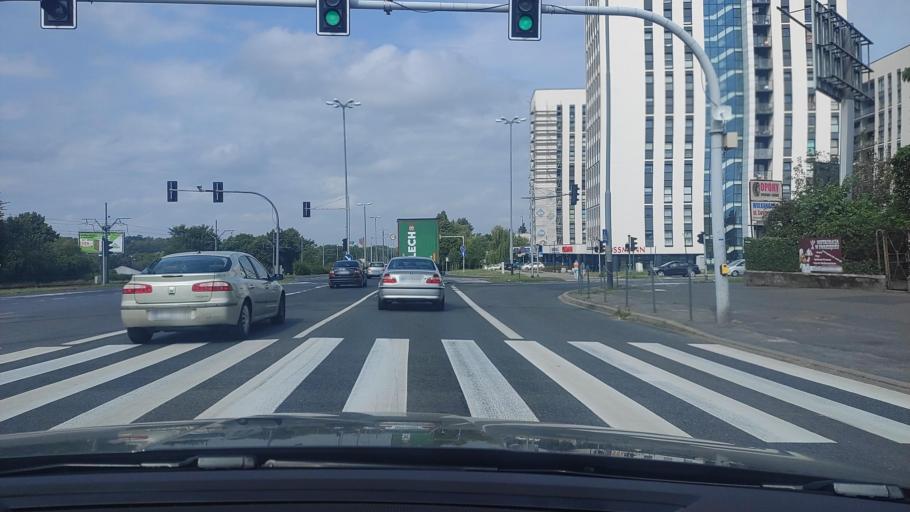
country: PL
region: Greater Poland Voivodeship
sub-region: Poznan
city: Poznan
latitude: 52.4099
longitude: 16.9810
